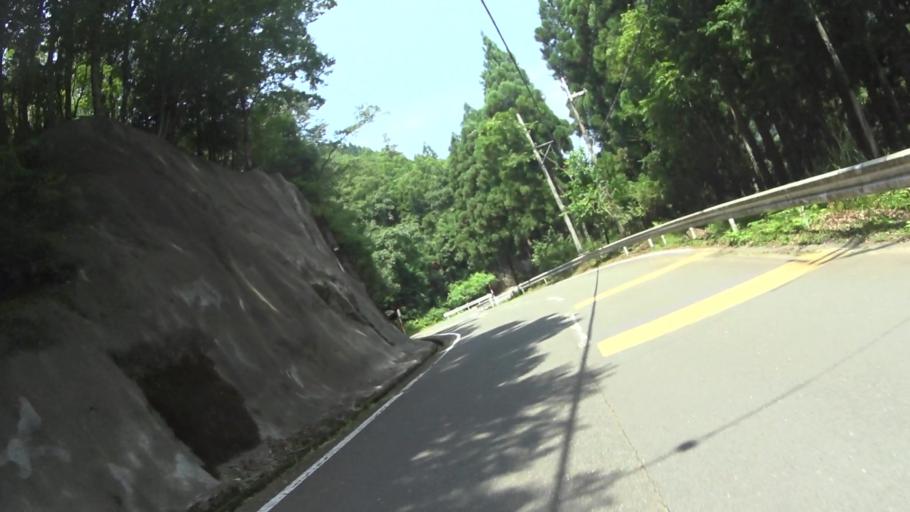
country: JP
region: Kyoto
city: Ayabe
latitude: 35.2805
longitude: 135.4305
